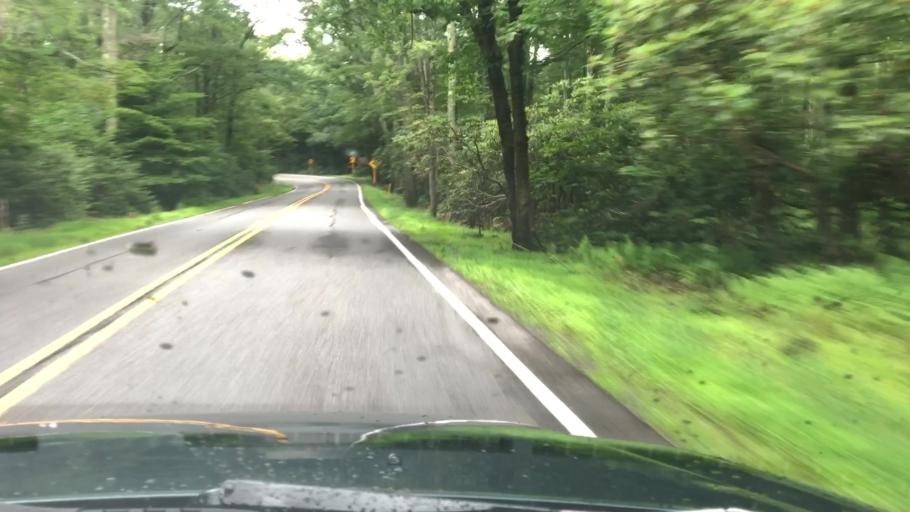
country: US
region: Pennsylvania
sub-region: Monroe County
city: Mountainhome
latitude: 41.2983
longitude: -75.2155
